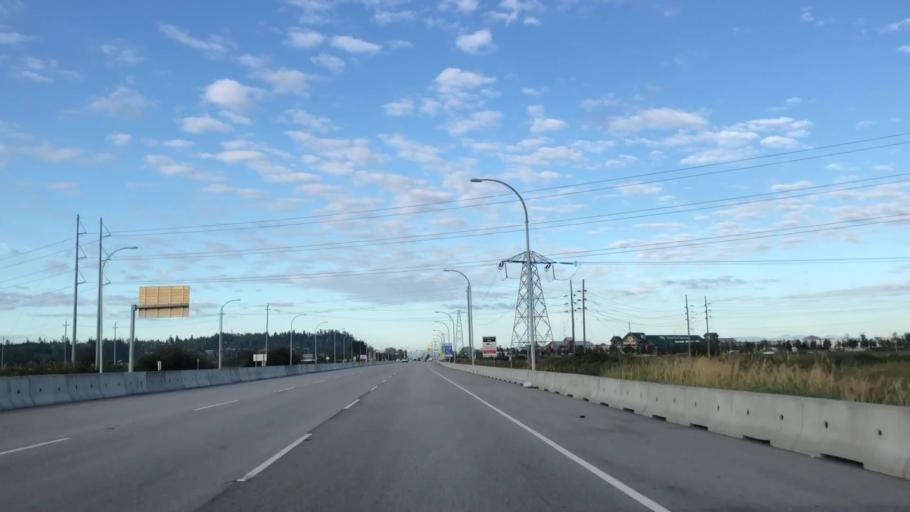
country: CA
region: British Columbia
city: Ladner
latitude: 49.0408
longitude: -123.0734
